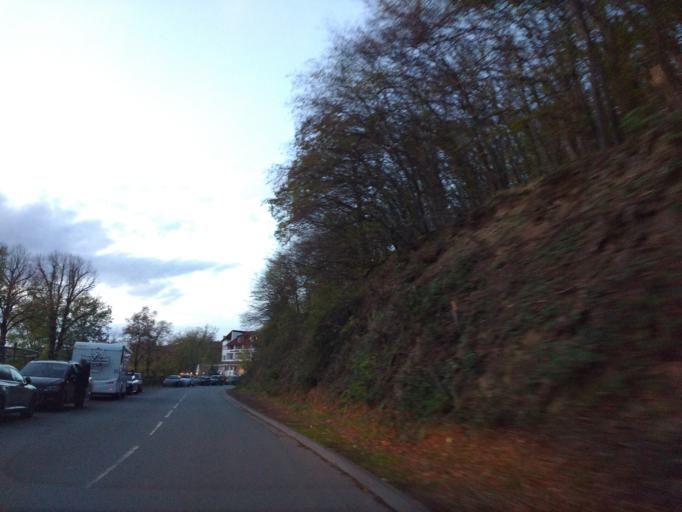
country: DE
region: Hesse
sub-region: Regierungsbezirk Kassel
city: Waldeck
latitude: 51.1856
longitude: 9.0604
